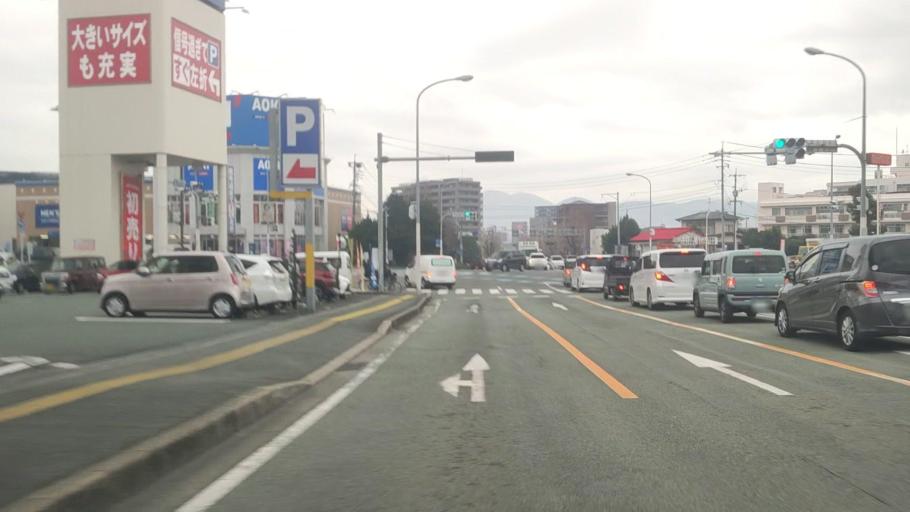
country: JP
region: Kumamoto
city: Kumamoto
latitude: 32.8072
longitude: 130.7488
